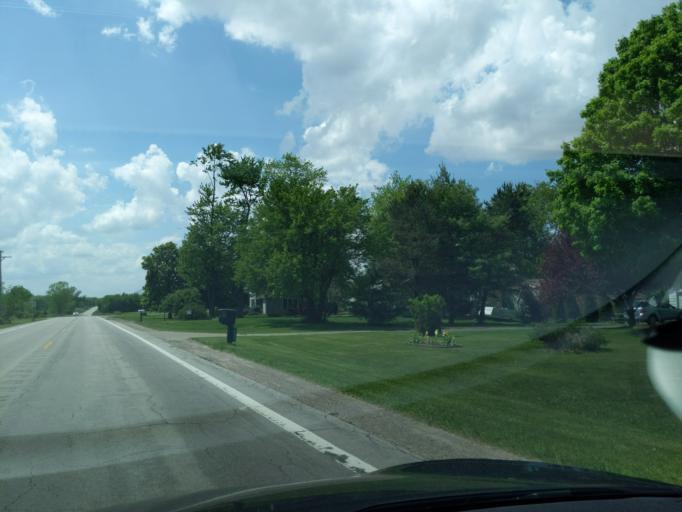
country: US
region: Michigan
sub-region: Ingham County
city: Stockbridge
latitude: 42.5562
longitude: -84.2573
